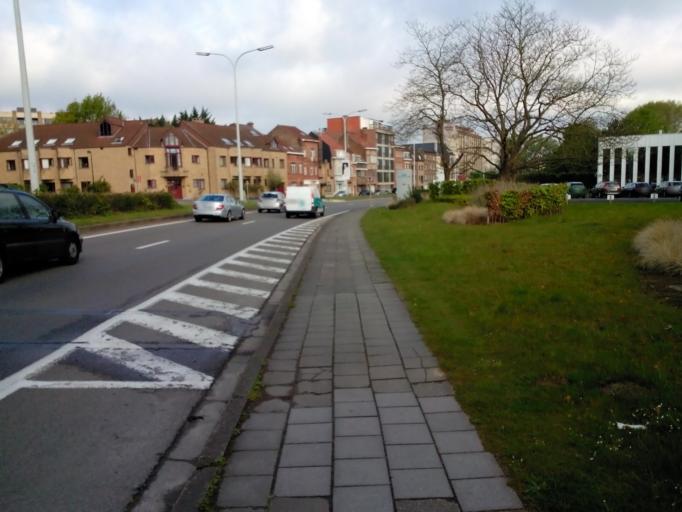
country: BE
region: Flanders
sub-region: Provincie Vlaams-Brabant
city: Diegem
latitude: 50.8726
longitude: 4.4156
